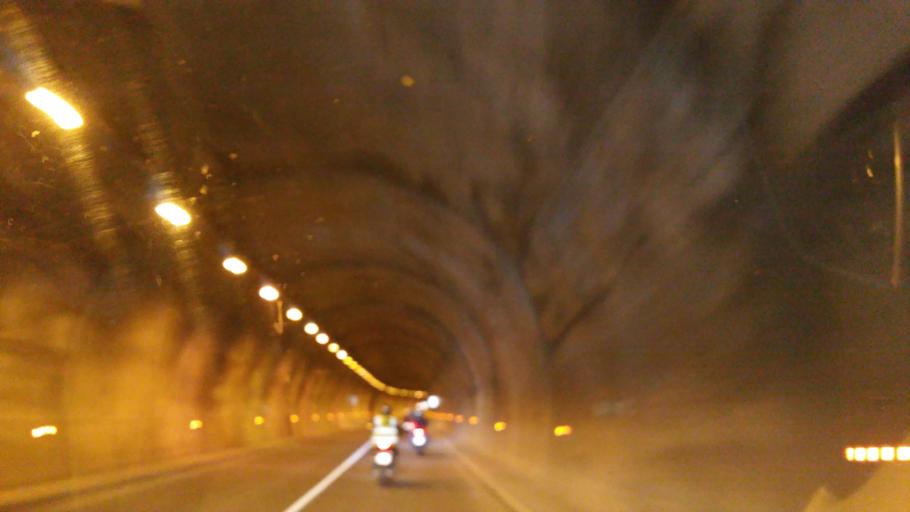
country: FR
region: Rhone-Alpes
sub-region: Departement de la Savoie
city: Val-d'Isere
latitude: 45.4718
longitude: 6.9543
